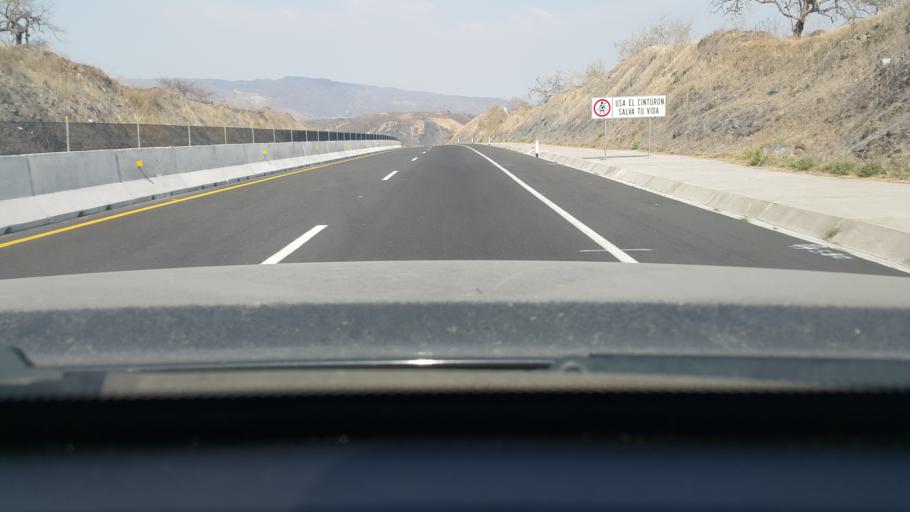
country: MX
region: Nayarit
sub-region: Ahuacatlan
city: Ahuacatlan
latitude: 21.0671
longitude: -104.4668
